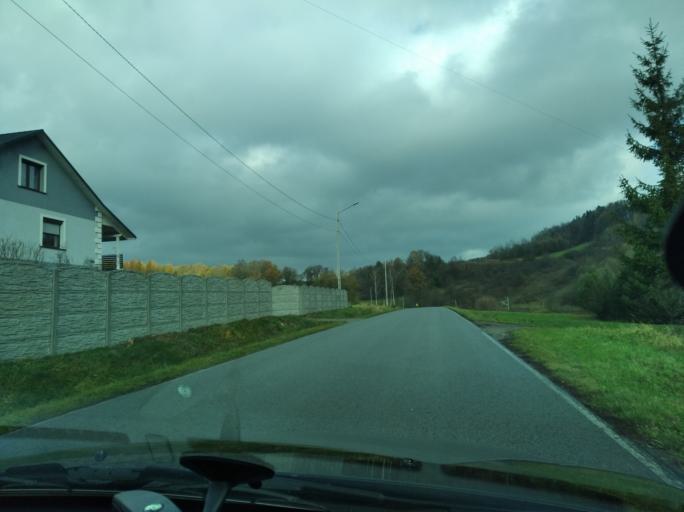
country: PL
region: Subcarpathian Voivodeship
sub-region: Powiat strzyzowski
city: Wisniowa
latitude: 49.9203
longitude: 21.7191
